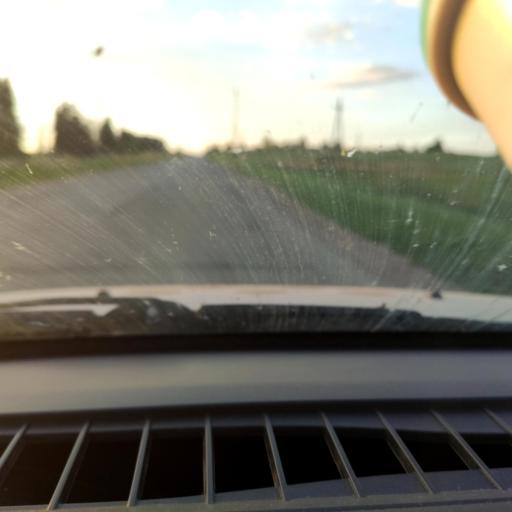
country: RU
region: Kirov
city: Kotel'nich
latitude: 58.5100
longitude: 48.2288
